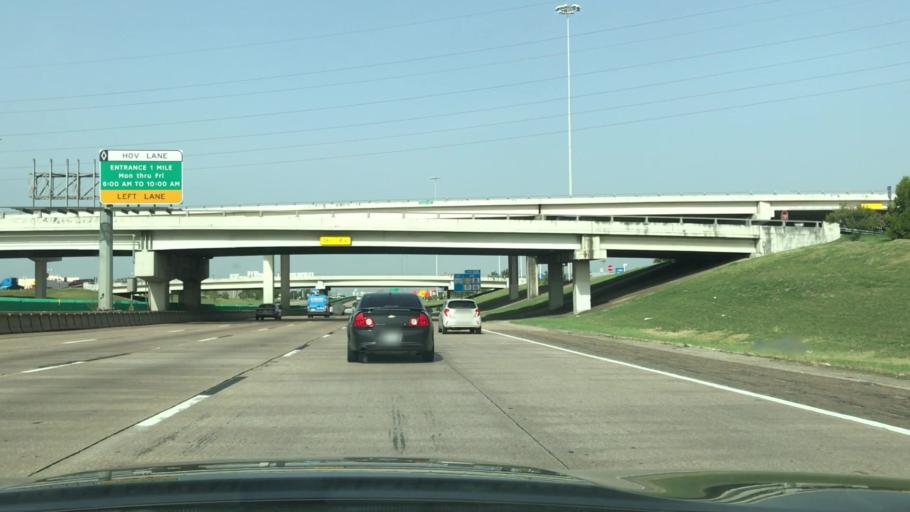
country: US
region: Texas
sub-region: Dallas County
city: Mesquite
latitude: 32.7986
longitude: -96.6813
